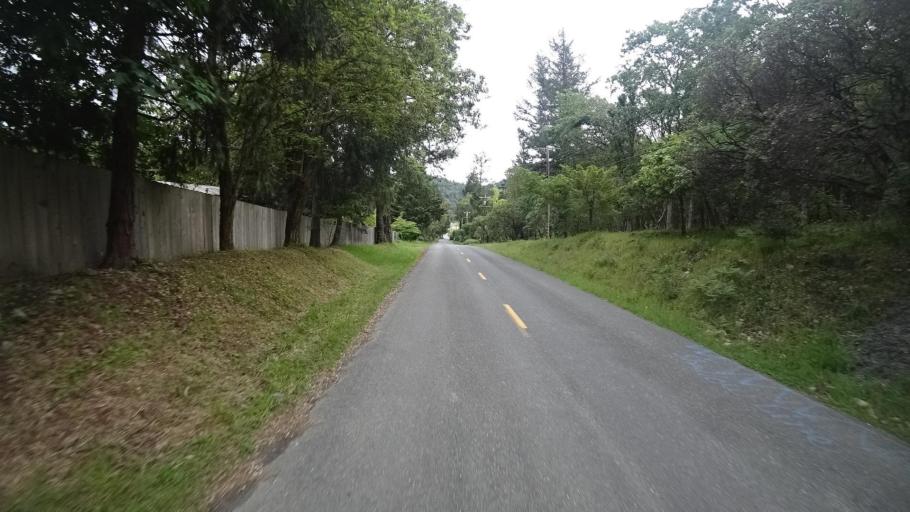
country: US
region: California
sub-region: Humboldt County
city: Willow Creek
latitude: 40.9698
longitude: -123.6305
